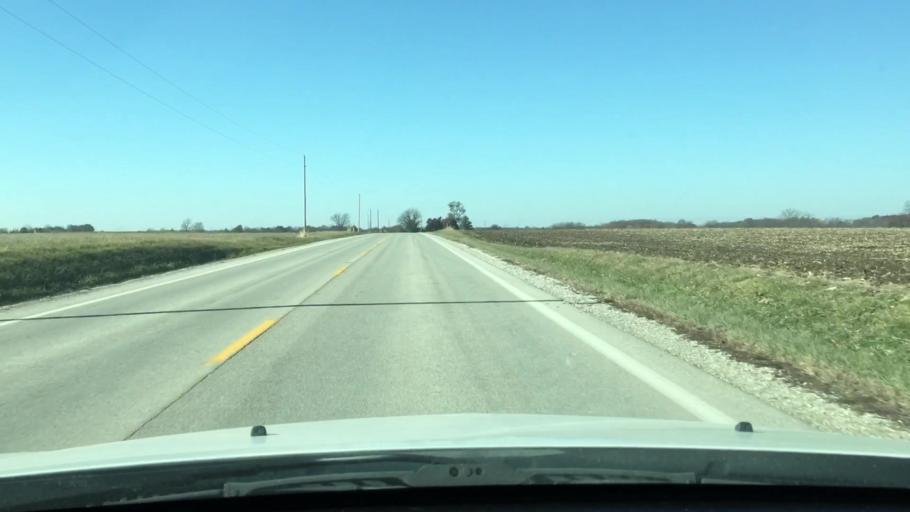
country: US
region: Illinois
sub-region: Pike County
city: Pittsfield
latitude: 39.6194
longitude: -90.7163
